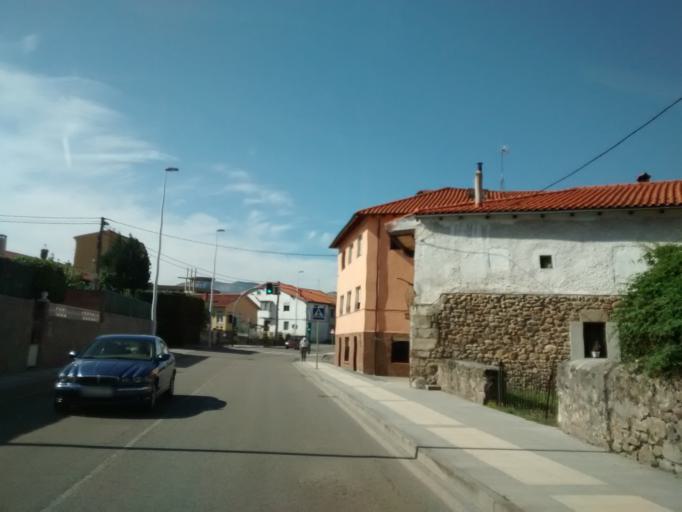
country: ES
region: Cantabria
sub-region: Provincia de Cantabria
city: Torrelavega
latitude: 43.3423
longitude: -4.0579
